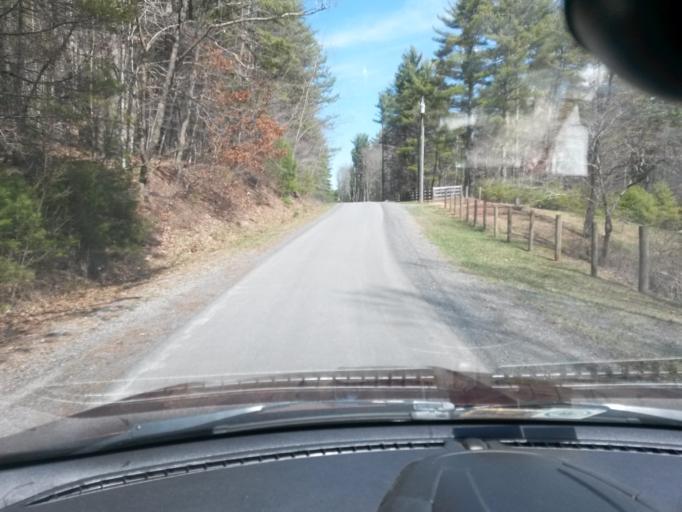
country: US
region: West Virginia
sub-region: Greenbrier County
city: Ronceverte
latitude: 37.6237
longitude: -80.3517
